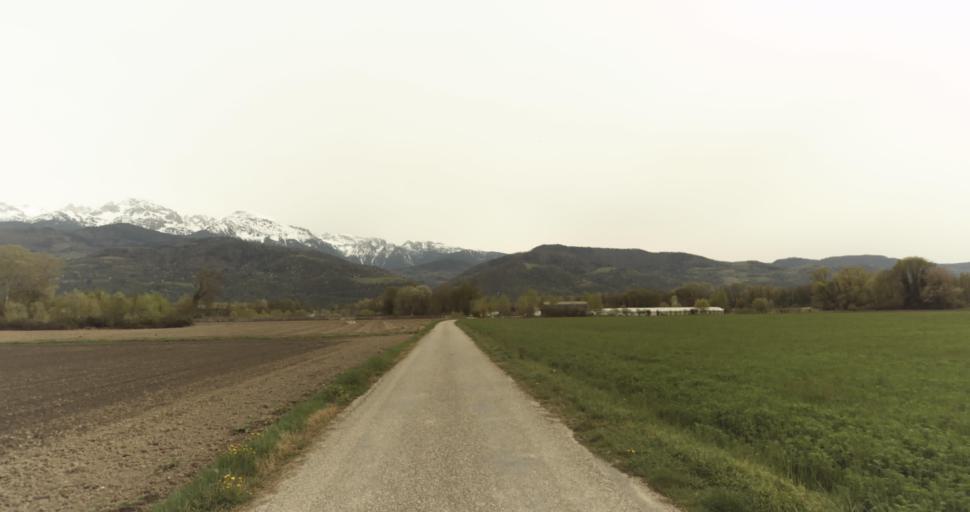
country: FR
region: Rhone-Alpes
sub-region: Departement de l'Isere
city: Montbonnot-Saint-Martin
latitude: 45.2229
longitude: 5.8253
